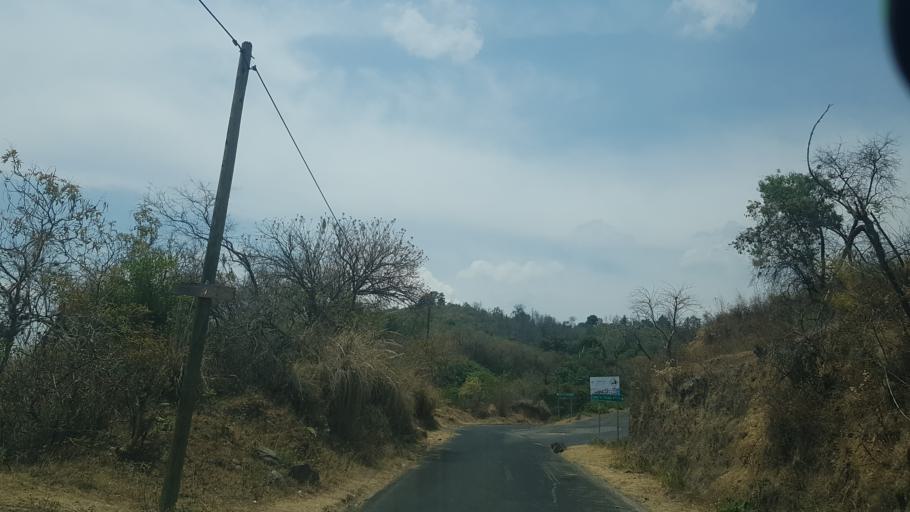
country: MX
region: Puebla
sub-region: Tochimilco
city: La Magdalena Yancuitlalpan
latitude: 18.8717
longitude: -98.6128
